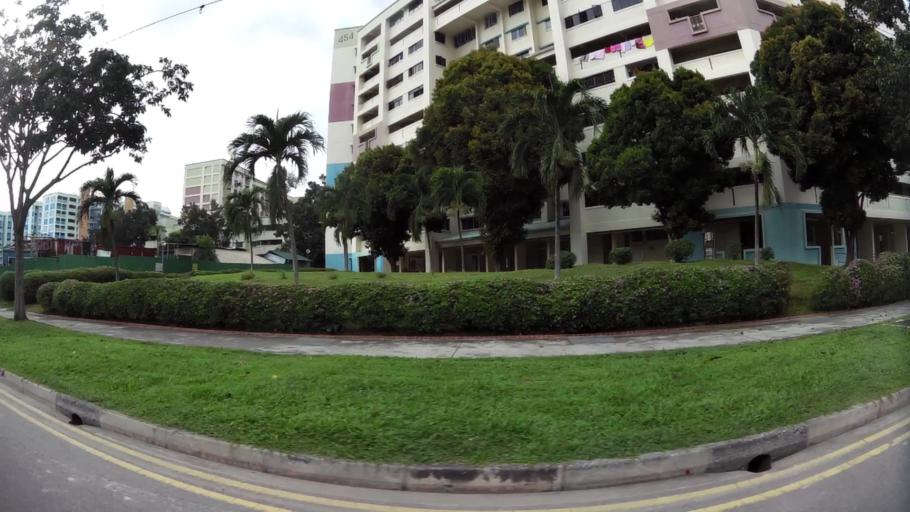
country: SG
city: Singapore
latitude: 1.3574
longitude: 103.9554
